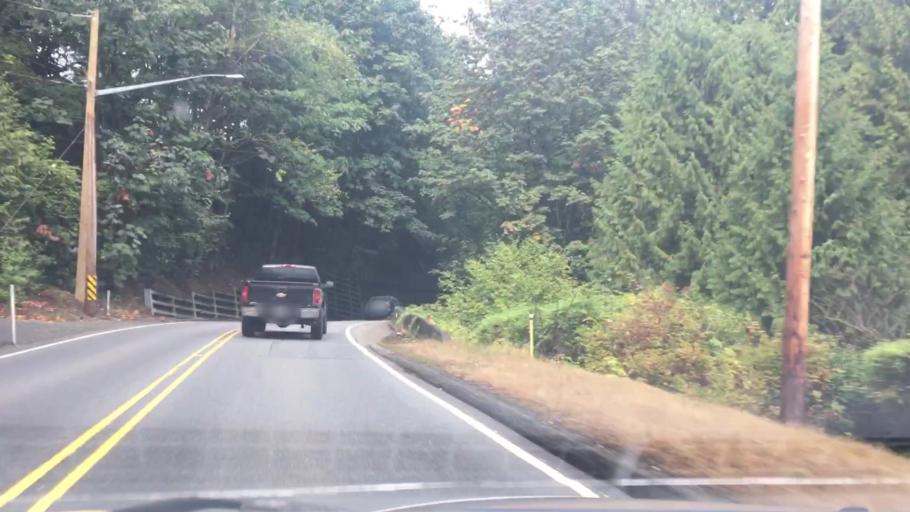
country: CA
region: British Columbia
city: Langley
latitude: 49.1026
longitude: -122.5499
